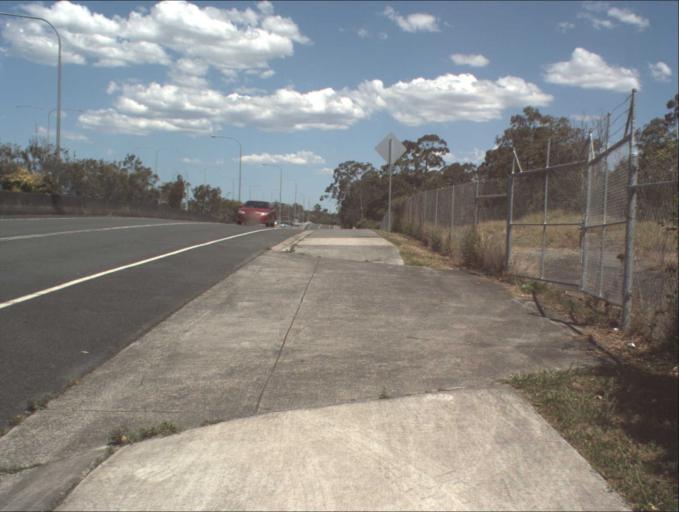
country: AU
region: Queensland
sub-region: Logan
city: Beenleigh
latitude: -27.7027
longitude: 153.1992
